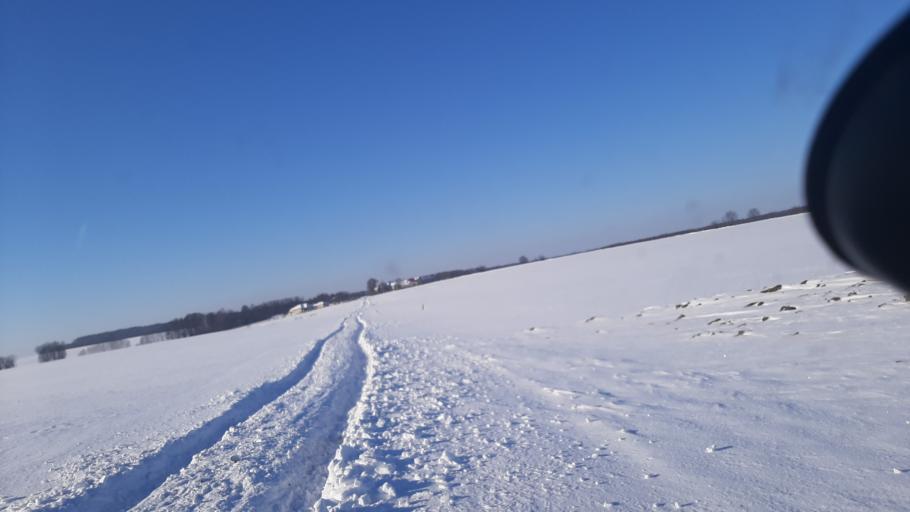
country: PL
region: Lublin Voivodeship
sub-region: Powiat lubelski
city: Jastkow
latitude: 51.3810
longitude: 22.4282
